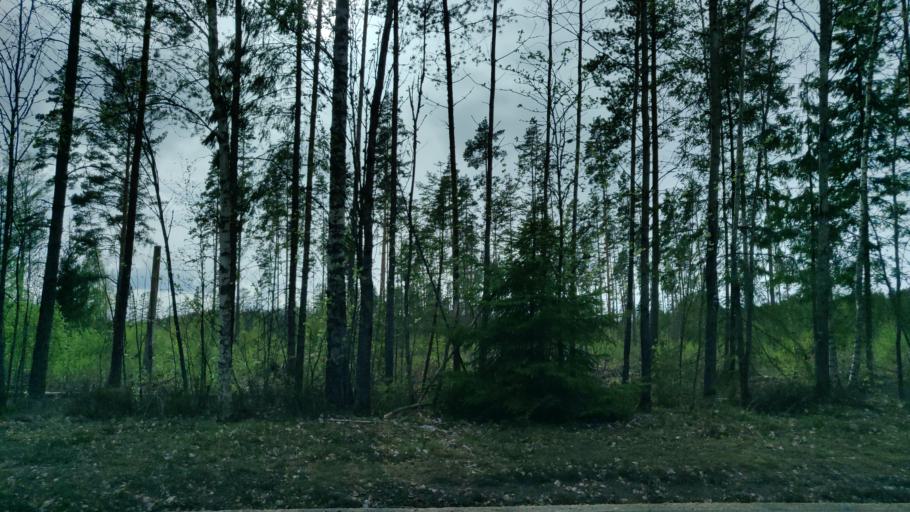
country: SE
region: Vaermland
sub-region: Forshaga Kommun
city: Deje
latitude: 59.6342
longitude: 13.4428
